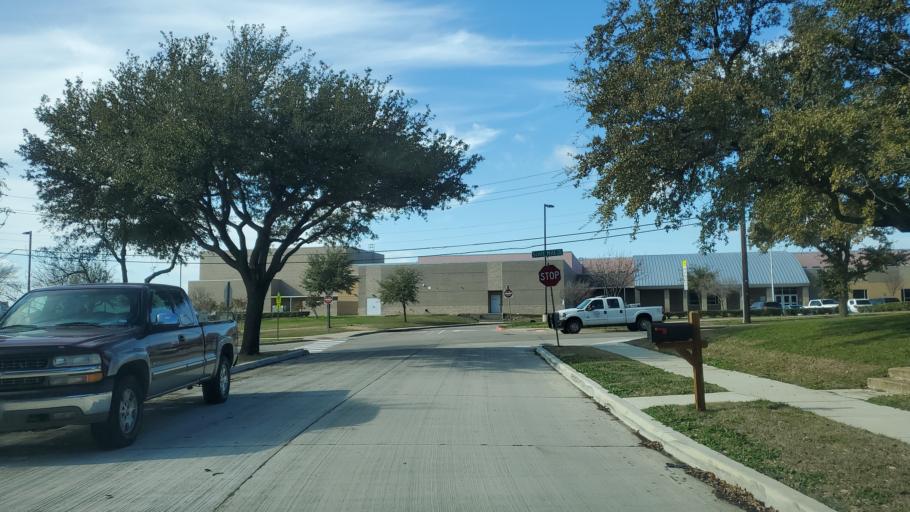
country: US
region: Texas
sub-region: Dallas County
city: Carrollton
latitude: 32.9942
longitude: -96.8793
